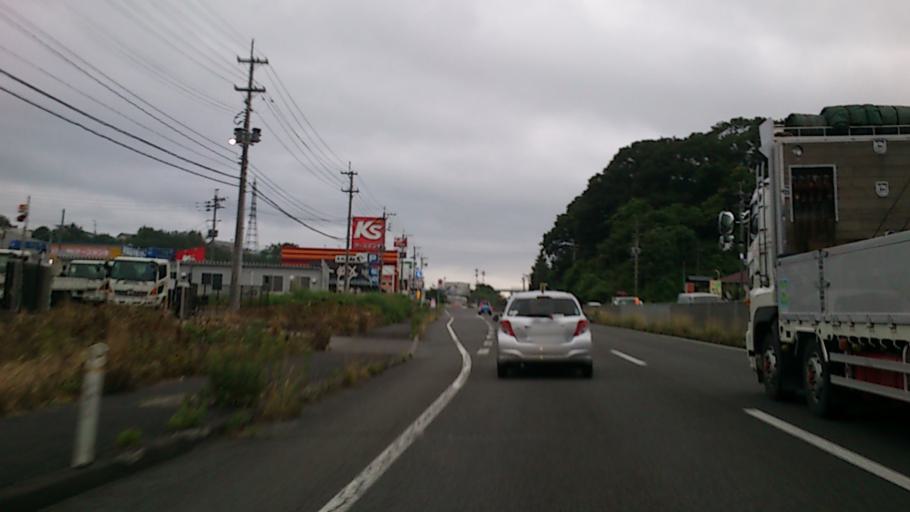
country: JP
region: Fukushima
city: Nihommatsu
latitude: 37.5779
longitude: 140.4216
